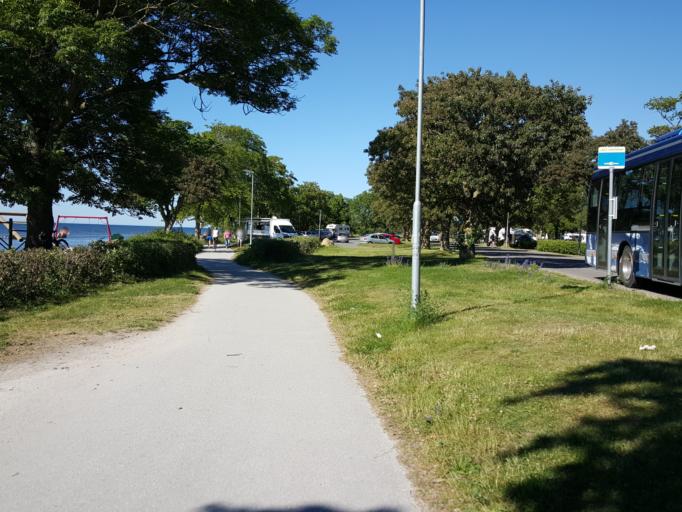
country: SE
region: Gotland
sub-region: Gotland
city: Visby
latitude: 57.6533
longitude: 18.3045
